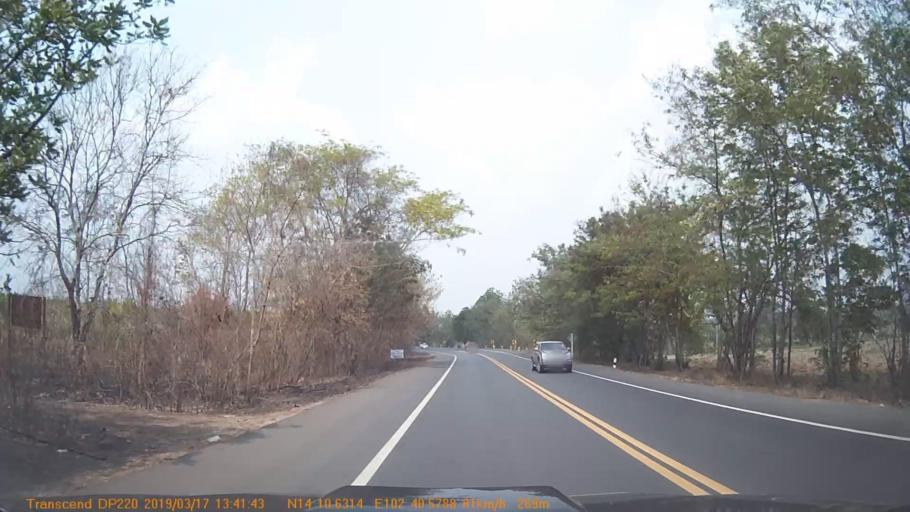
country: TH
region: Buriram
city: Non Din Daeng
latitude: 14.1773
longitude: 102.6763
